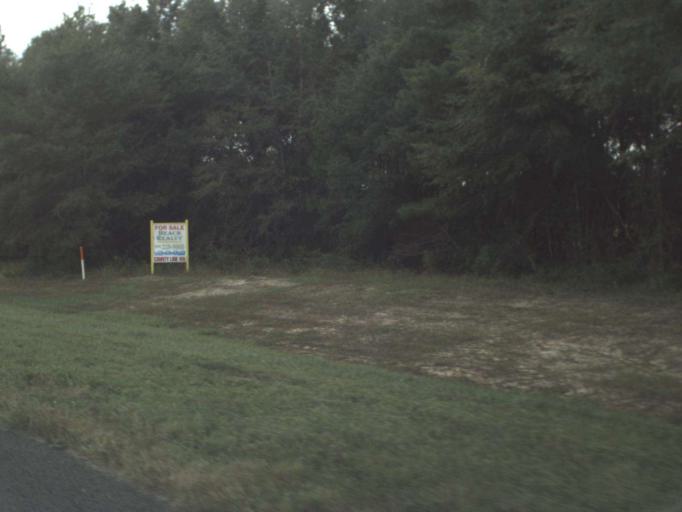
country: US
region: Florida
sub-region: Bay County
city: Youngstown
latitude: 30.5693
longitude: -85.3879
